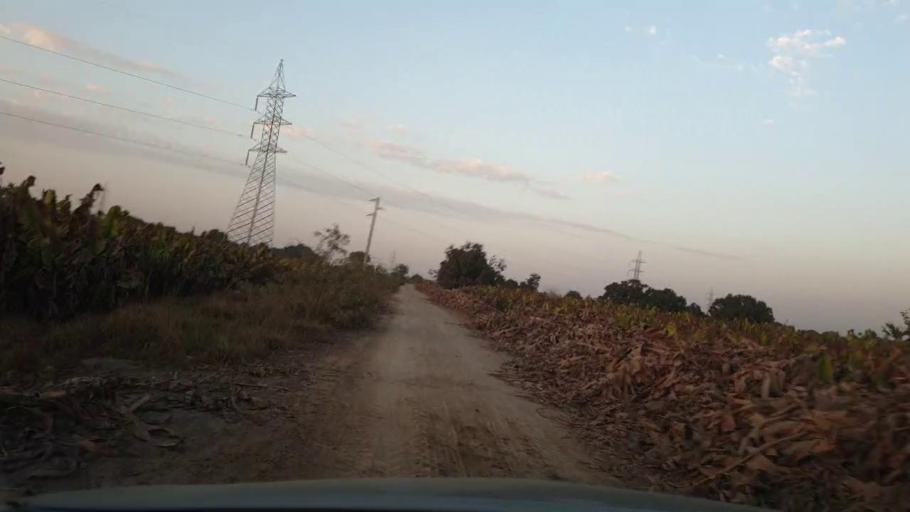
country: PK
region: Sindh
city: Matiari
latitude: 25.6163
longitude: 68.4844
